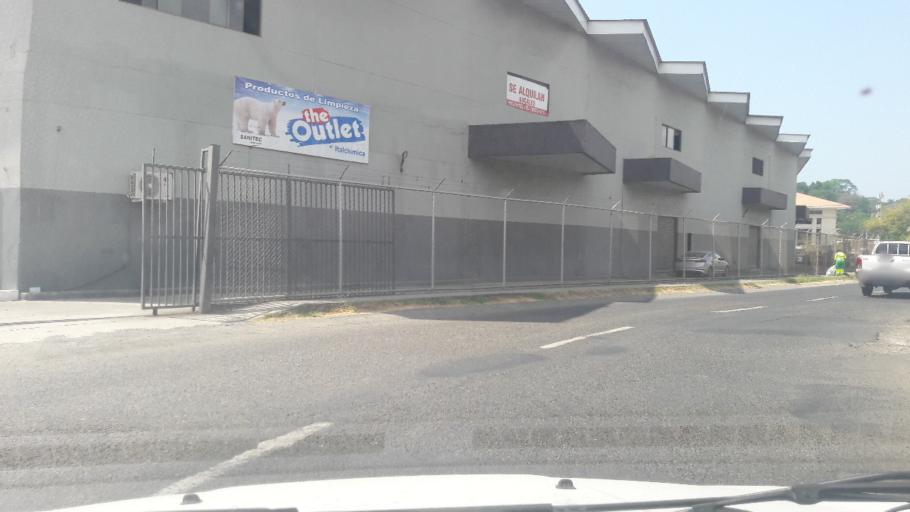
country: PA
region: Panama
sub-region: Distrito de Panama
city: Ancon
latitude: 8.9704
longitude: -79.5476
